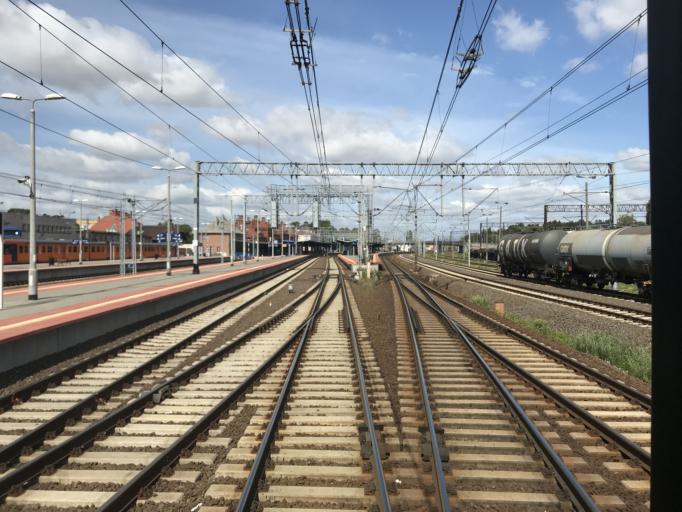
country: PL
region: Pomeranian Voivodeship
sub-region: Powiat malborski
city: Malbork
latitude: 54.0354
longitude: 19.0457
